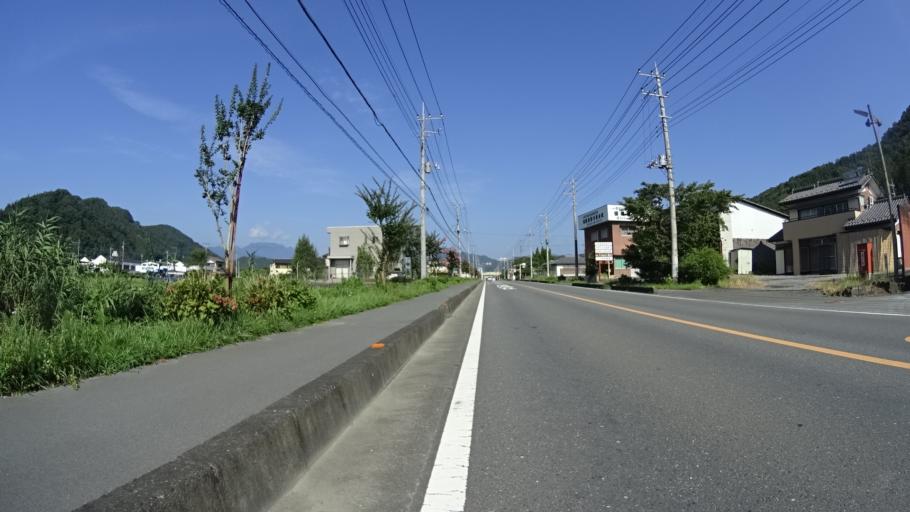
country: JP
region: Saitama
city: Chichibu
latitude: 36.0166
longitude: 139.0169
